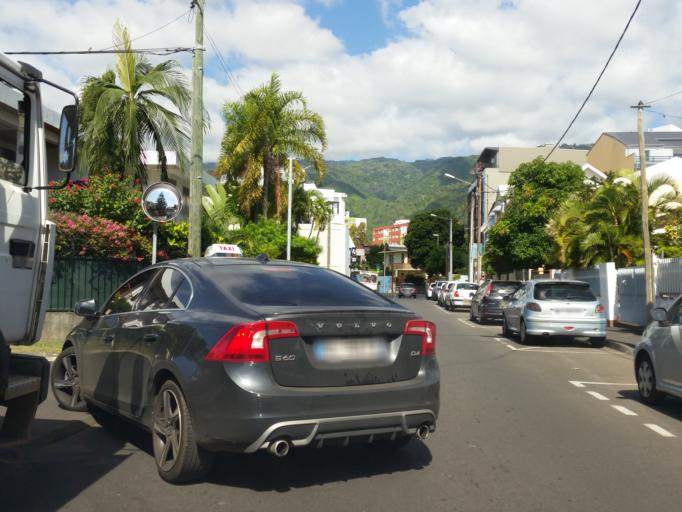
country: RE
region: Reunion
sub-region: Reunion
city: Saint-Denis
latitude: -20.8875
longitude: 55.4584
